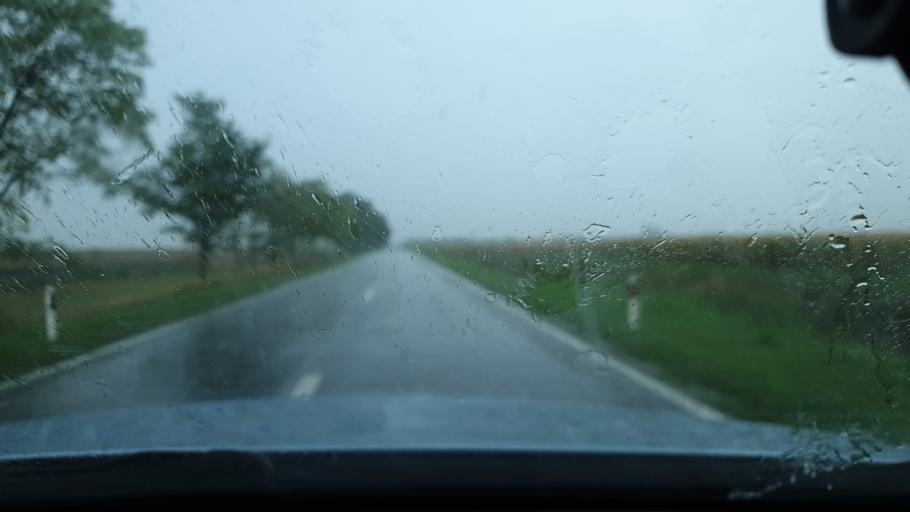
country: RS
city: Lazarevo
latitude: 45.3907
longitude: 20.5634
